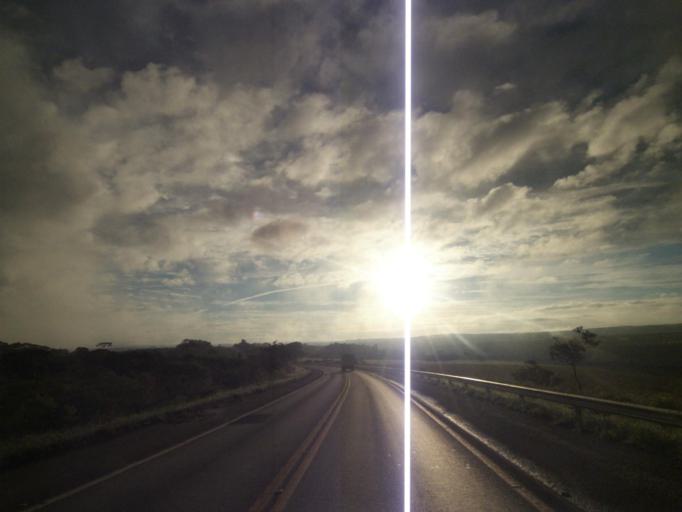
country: BR
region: Goias
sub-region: Pirenopolis
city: Pirenopolis
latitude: -15.7680
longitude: -48.7185
